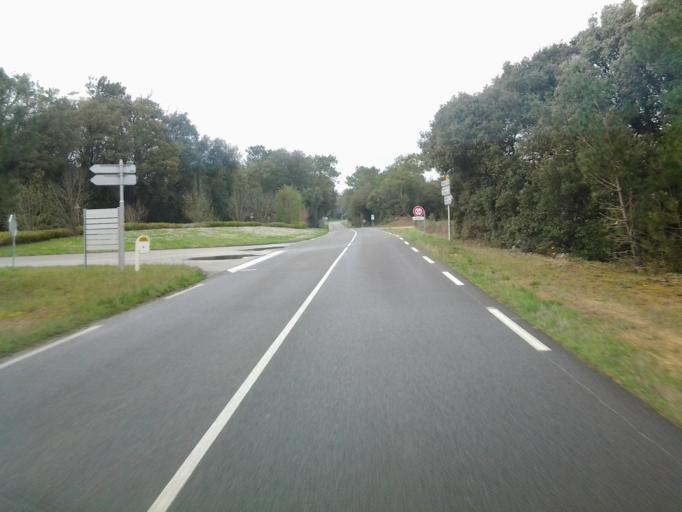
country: FR
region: Pays de la Loire
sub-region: Departement de la Vendee
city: La Tranche-sur-Mer
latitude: 46.3734
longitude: -1.4620
